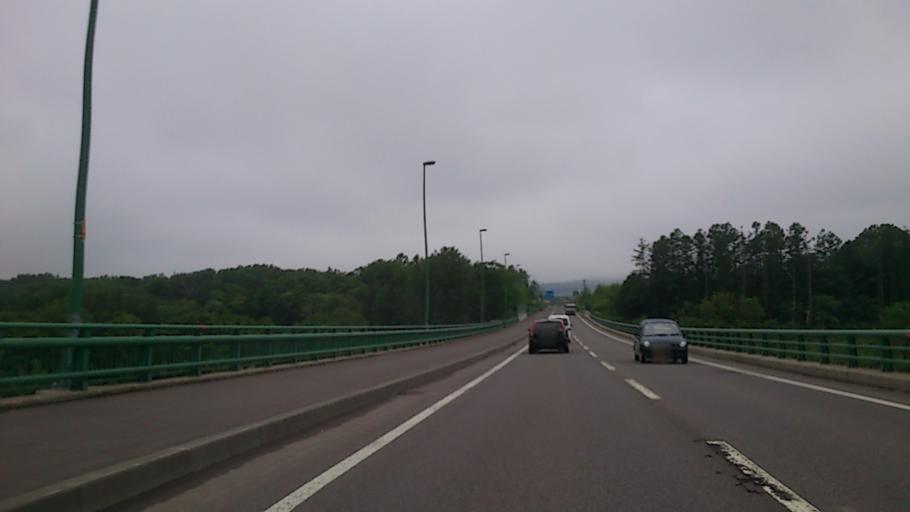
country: JP
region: Hokkaido
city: Niseko Town
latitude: 42.8650
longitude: 140.7323
